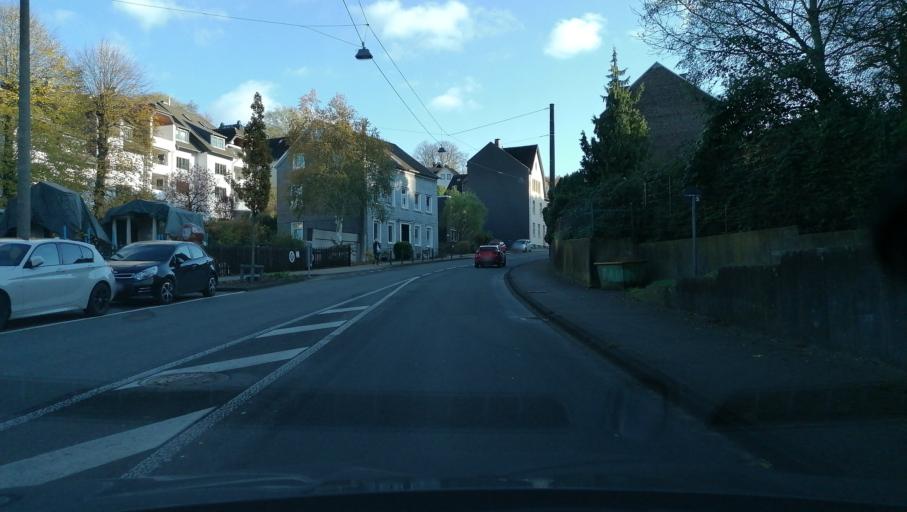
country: DE
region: North Rhine-Westphalia
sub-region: Regierungsbezirk Arnsberg
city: Schwelm
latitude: 51.2815
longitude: 7.2929
